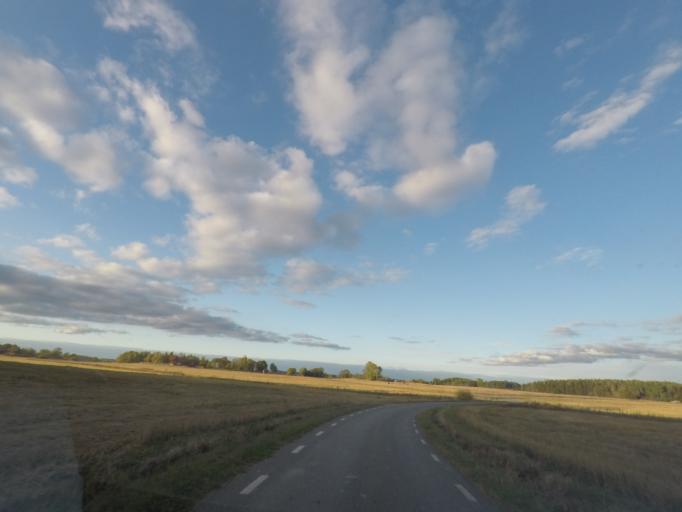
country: SE
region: Vaestmanland
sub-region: Kungsors Kommun
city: Kungsoer
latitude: 59.5127
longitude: 16.1120
